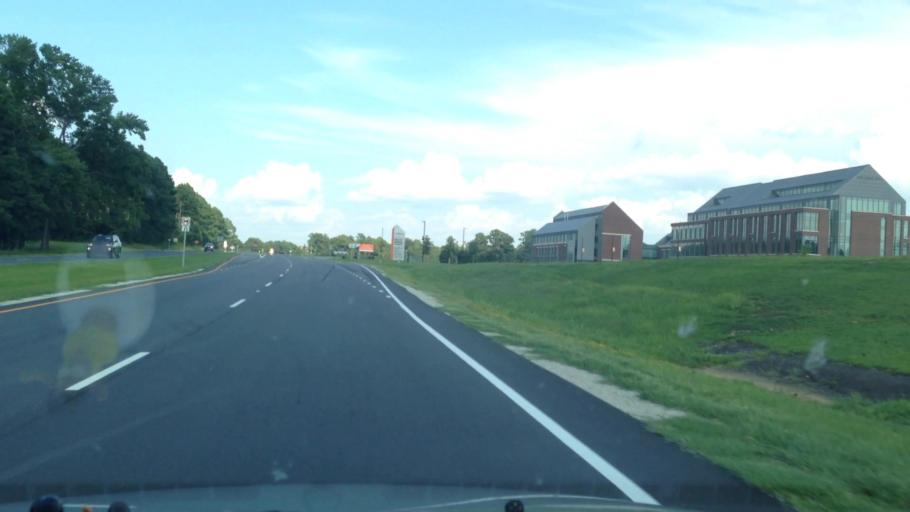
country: US
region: North Carolina
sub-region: Harnett County
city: Buies Creek
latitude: 35.4069
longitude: -78.7599
